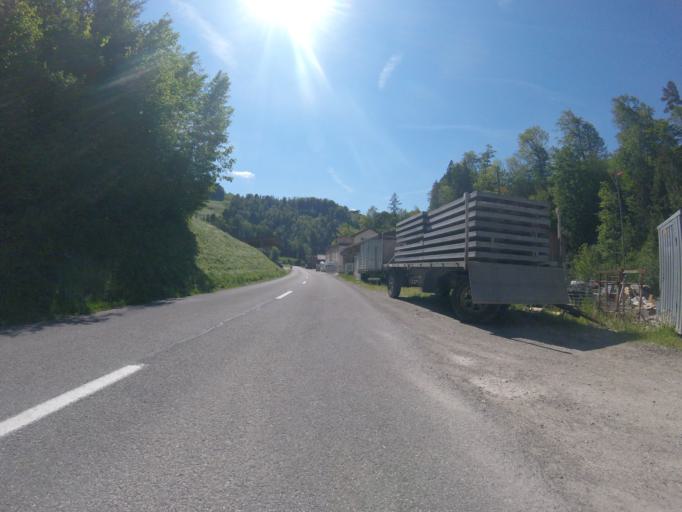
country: CH
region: Saint Gallen
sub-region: Wahlkreis Toggenburg
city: Mogelsberg
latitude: 47.3652
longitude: 9.1265
